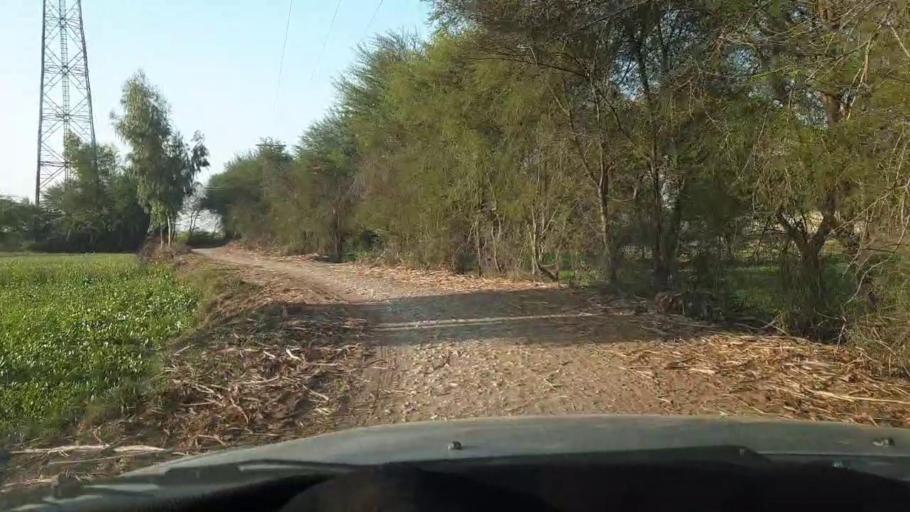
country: PK
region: Sindh
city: Mirpur Mathelo
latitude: 27.9875
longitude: 69.6288
